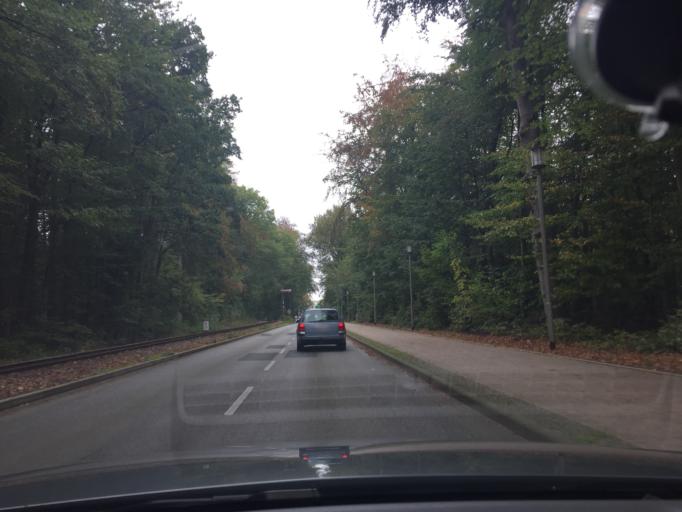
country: DE
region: Mecklenburg-Vorpommern
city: Bad Doberan
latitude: 54.1404
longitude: 11.8469
